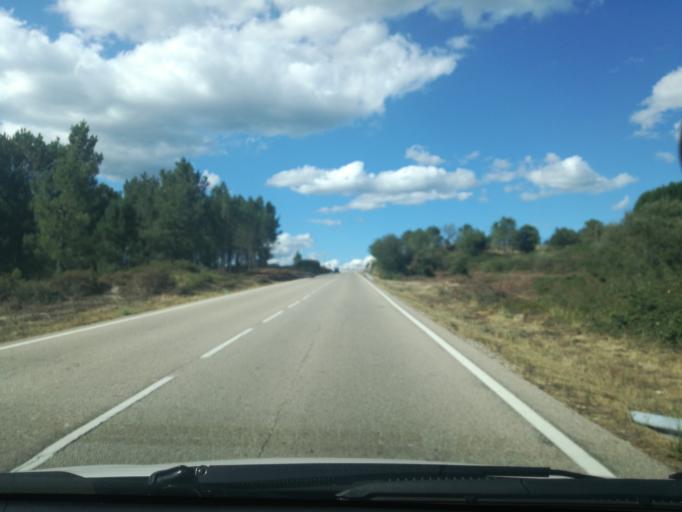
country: ES
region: Galicia
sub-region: Provincia de Ourense
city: Lobios
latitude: 41.8815
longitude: -8.0988
